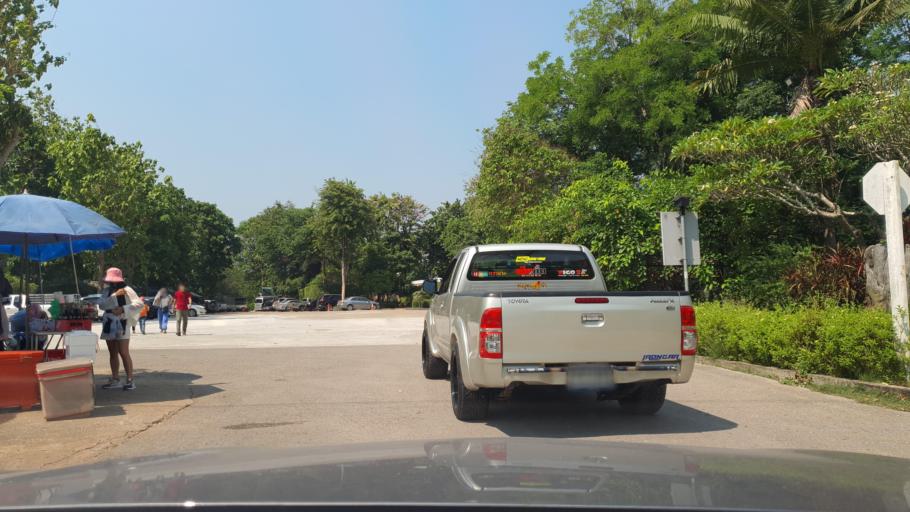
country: TH
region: Kanchanaburi
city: Sai Yok
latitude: 14.0996
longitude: 99.1699
